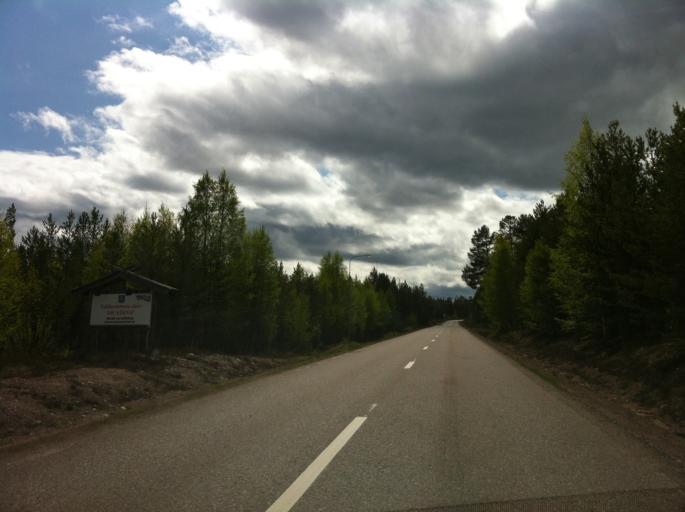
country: NO
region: Hedmark
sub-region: Trysil
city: Innbygda
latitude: 61.6847
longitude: 13.1280
